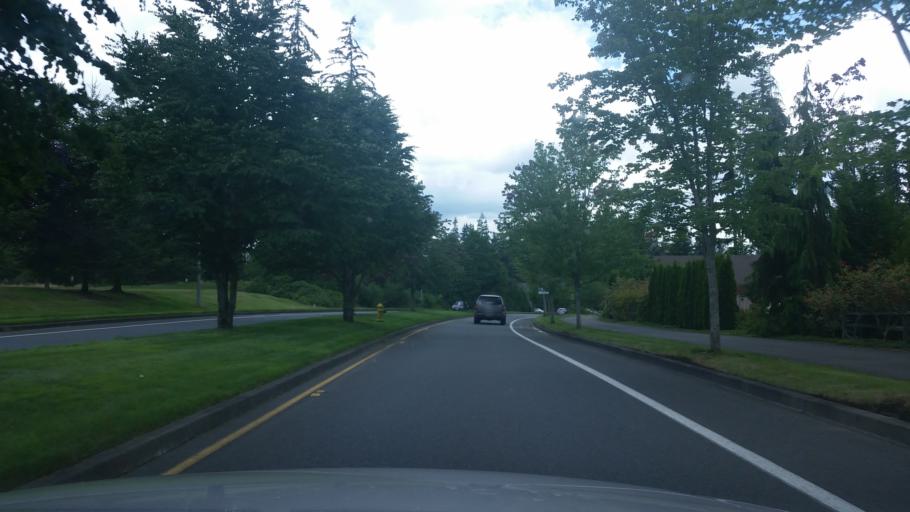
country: US
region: Washington
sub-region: King County
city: Union Hill-Novelty Hill
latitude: 47.7097
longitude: -122.0273
